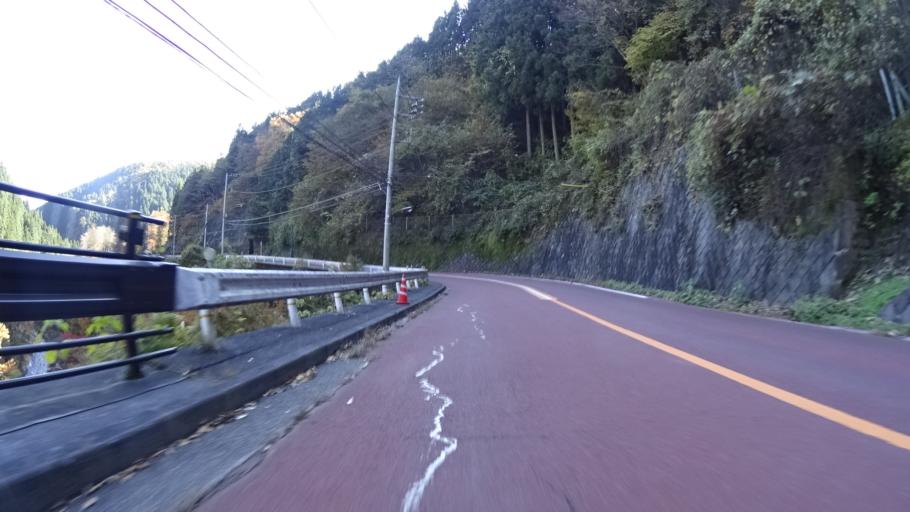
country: JP
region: Yamanashi
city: Uenohara
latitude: 35.7220
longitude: 139.0640
